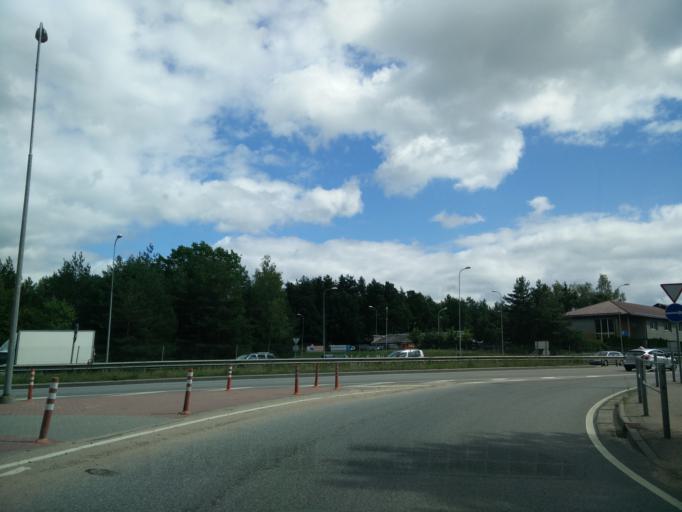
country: LT
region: Vilnius County
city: Pilaite
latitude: 54.6539
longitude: 25.1500
